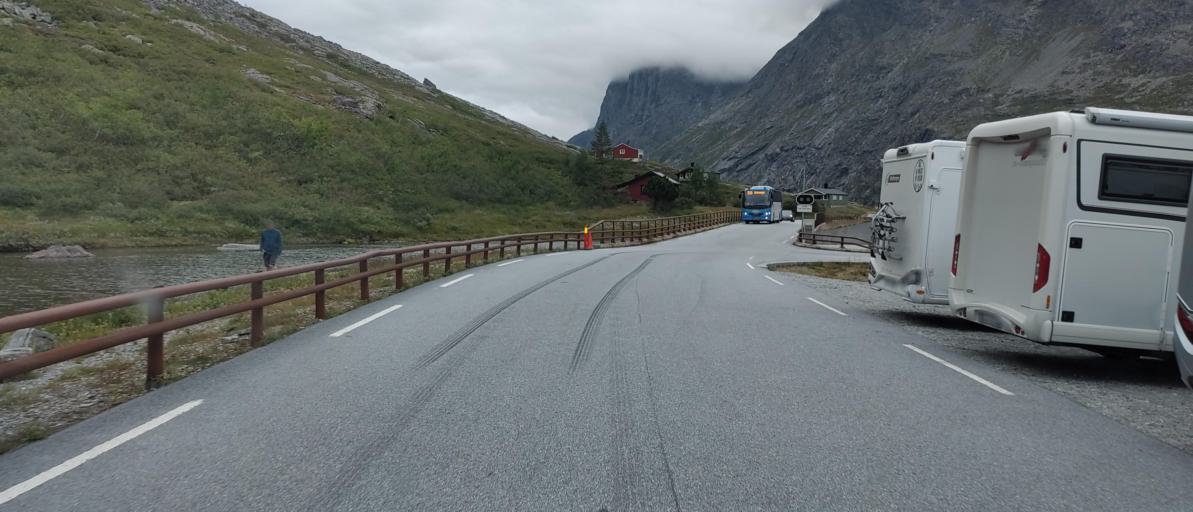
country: NO
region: More og Romsdal
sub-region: Rauma
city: Andalsnes
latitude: 62.4544
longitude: 7.6610
